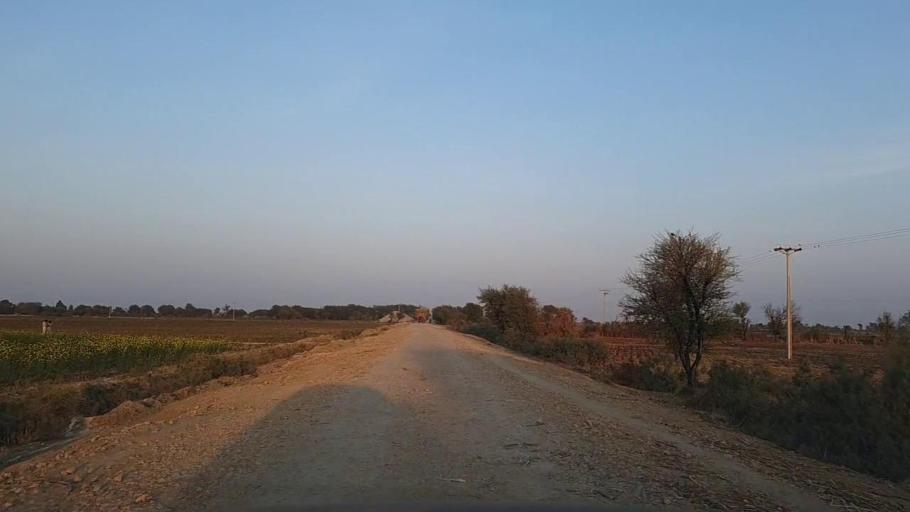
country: PK
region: Sindh
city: Tando Mittha Khan
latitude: 25.9722
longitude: 69.0920
